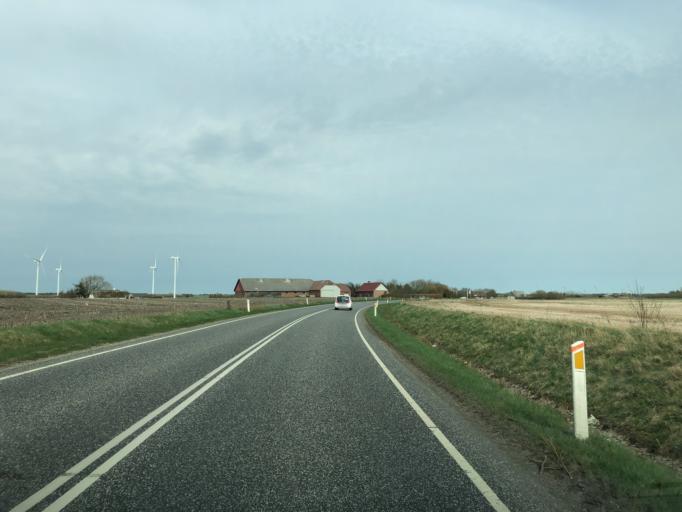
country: DK
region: South Denmark
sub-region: Varde Kommune
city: Oksbol
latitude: 55.8355
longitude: 8.3208
